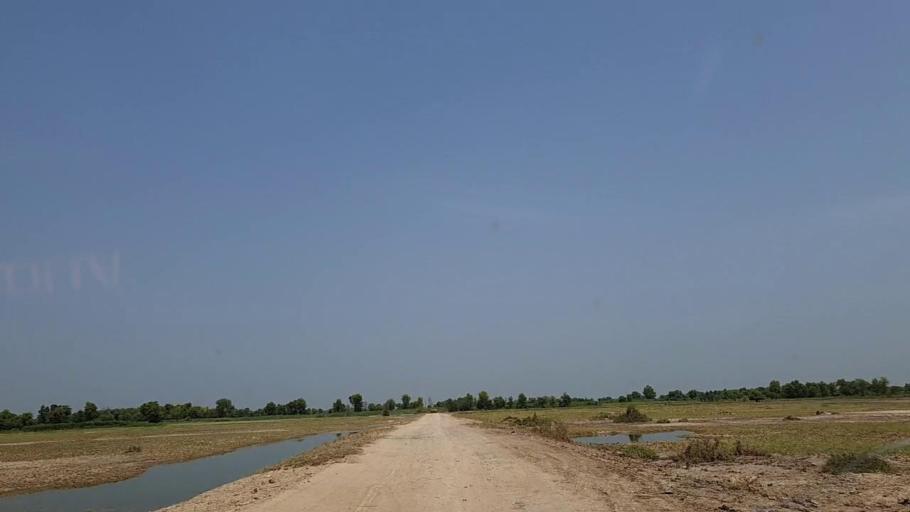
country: PK
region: Sindh
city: Ghotki
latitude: 27.9978
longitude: 69.4064
